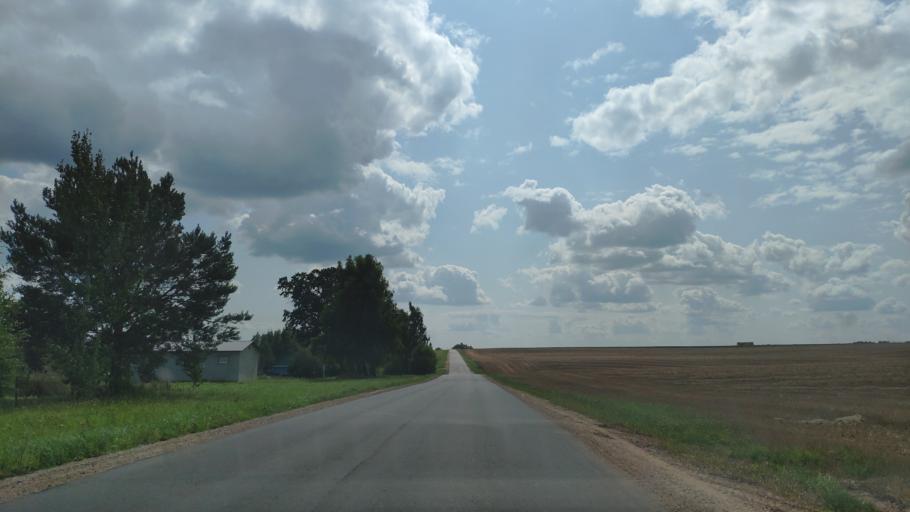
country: BY
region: Minsk
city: Khatsyezhyna
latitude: 53.8386
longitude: 27.3096
